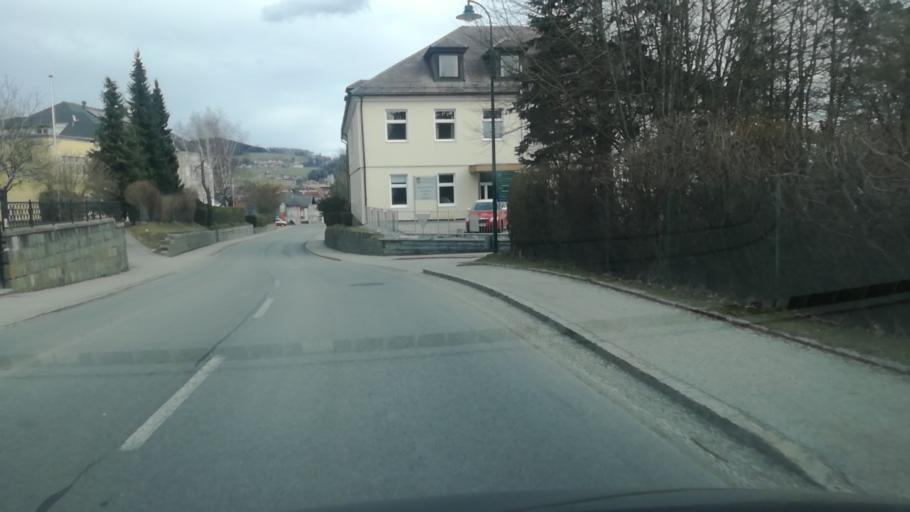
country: AT
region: Upper Austria
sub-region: Politischer Bezirk Vocklabruck
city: Frankenburg
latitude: 48.0672
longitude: 13.4851
